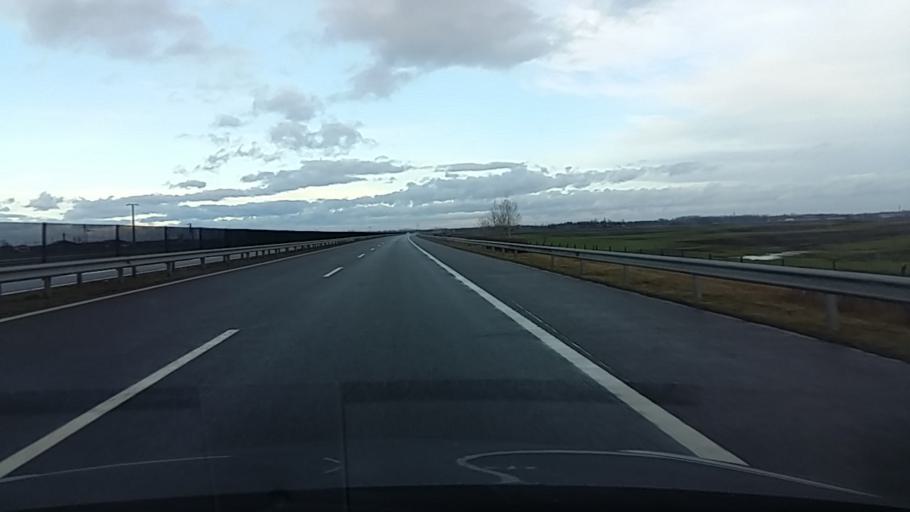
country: HU
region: Hajdu-Bihar
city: Hajdunanas
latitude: 47.8494
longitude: 21.3479
